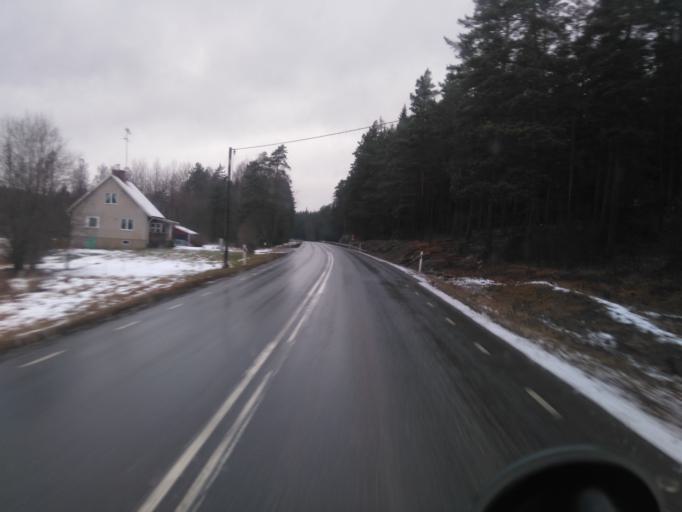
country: SE
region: Joenkoeping
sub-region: Eksjo Kommun
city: Haljarp
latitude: 57.6264
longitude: 15.4464
